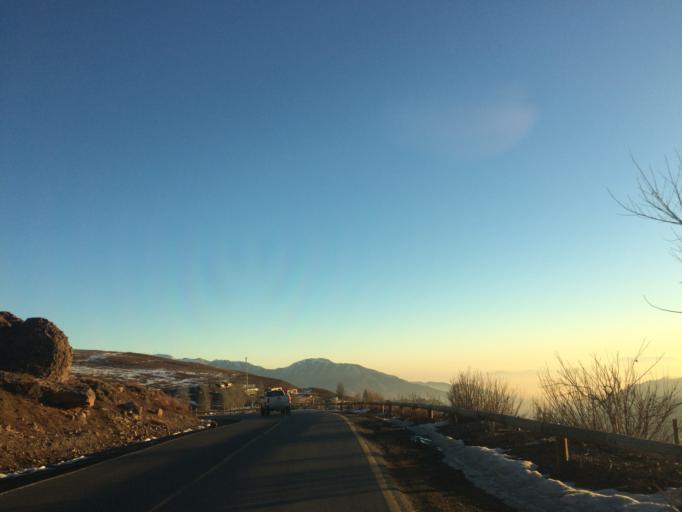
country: CL
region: Santiago Metropolitan
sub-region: Provincia de Santiago
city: Villa Presidente Frei, Nunoa, Santiago, Chile
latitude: -33.3413
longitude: -70.2952
